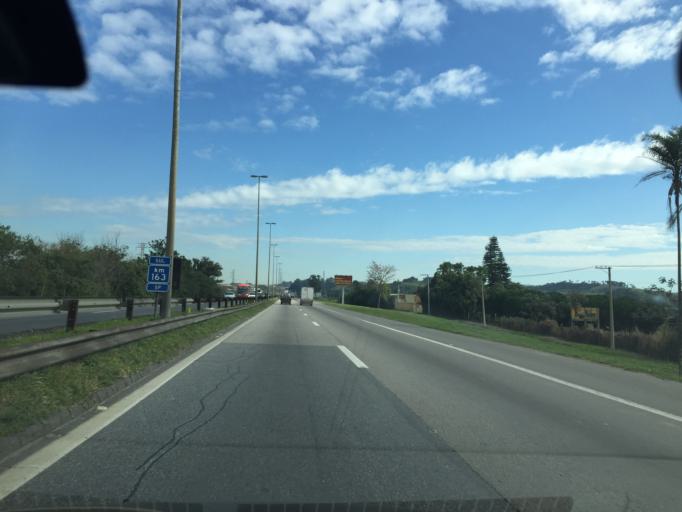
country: BR
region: Sao Paulo
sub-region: Jacarei
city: Jacarei
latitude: -23.2850
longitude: -45.9898
